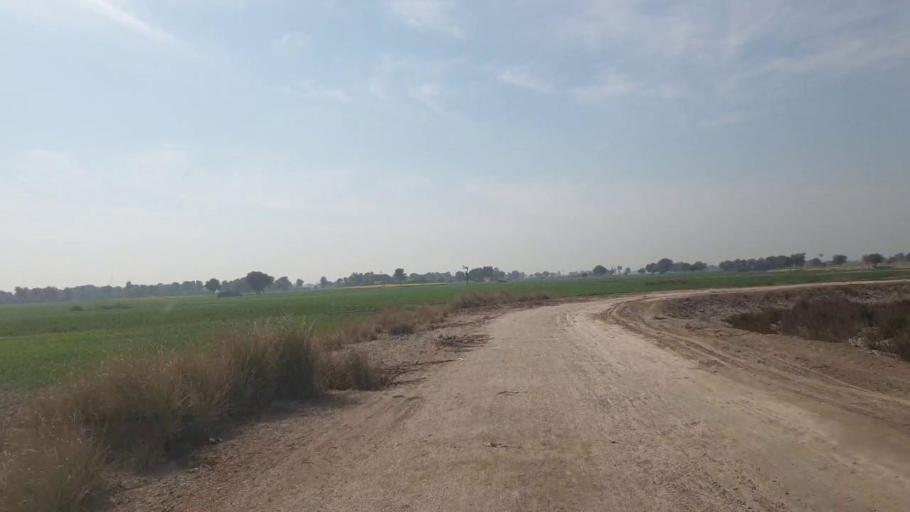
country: PK
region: Sindh
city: Nawabshah
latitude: 26.1630
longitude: 68.5115
